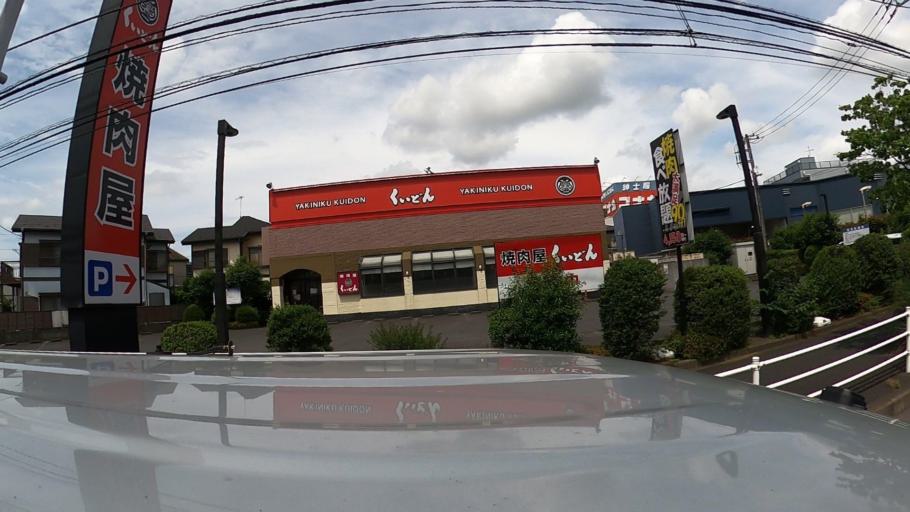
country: JP
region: Kanagawa
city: Fujisawa
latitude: 35.4071
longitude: 139.4699
